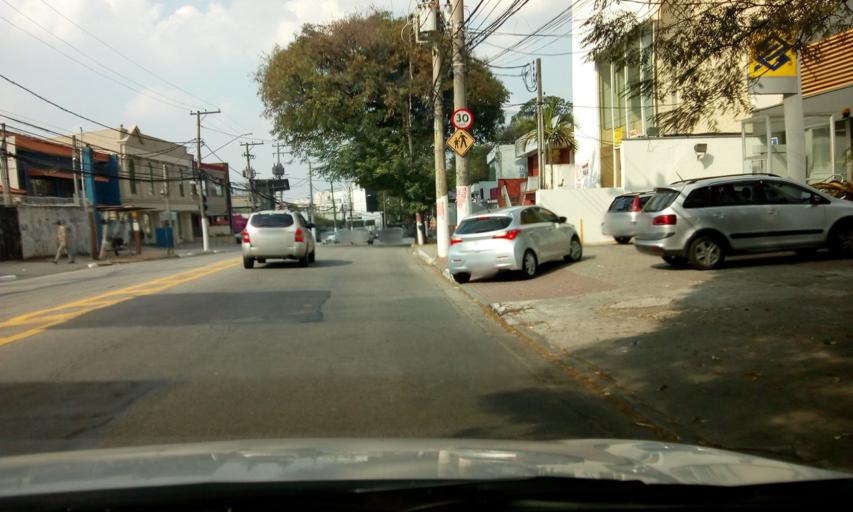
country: BR
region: Sao Paulo
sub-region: Sao Paulo
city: Sao Paulo
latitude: -23.5357
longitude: -46.7109
